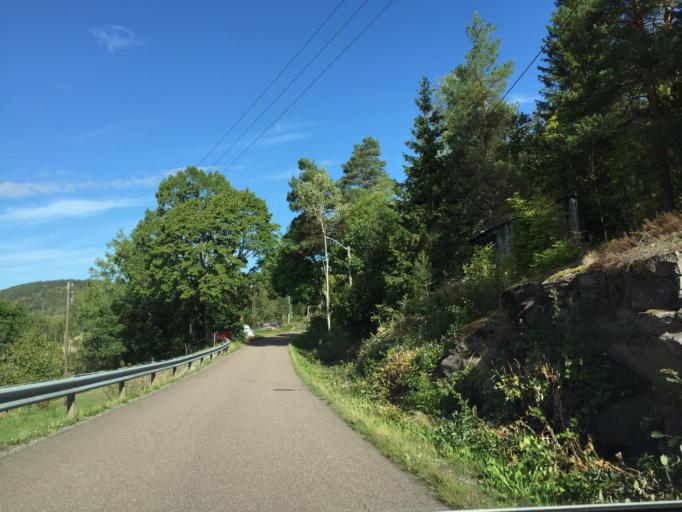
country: NO
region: Vestfold
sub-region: Holmestrand
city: Gullhaug
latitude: 59.4773
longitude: 10.1793
